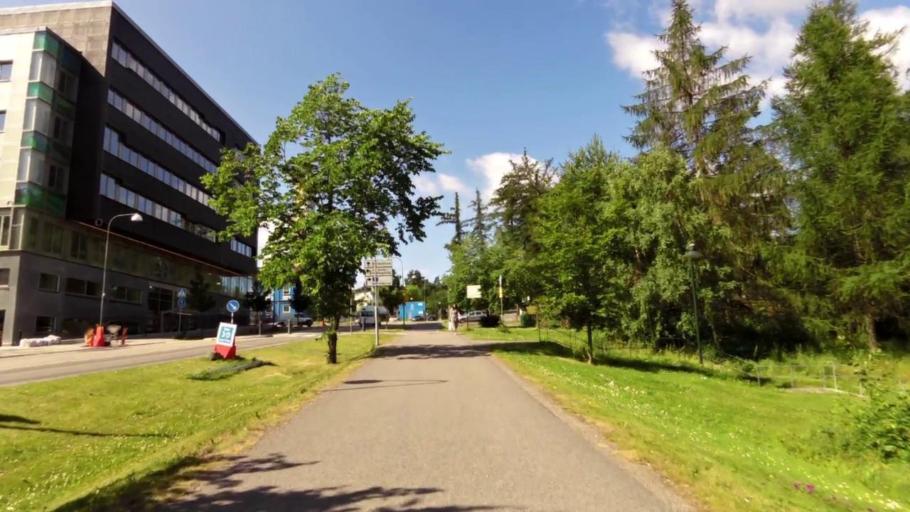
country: SE
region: OEstergoetland
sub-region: Linkopings Kommun
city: Linkoping
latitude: 58.4041
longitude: 15.6225
